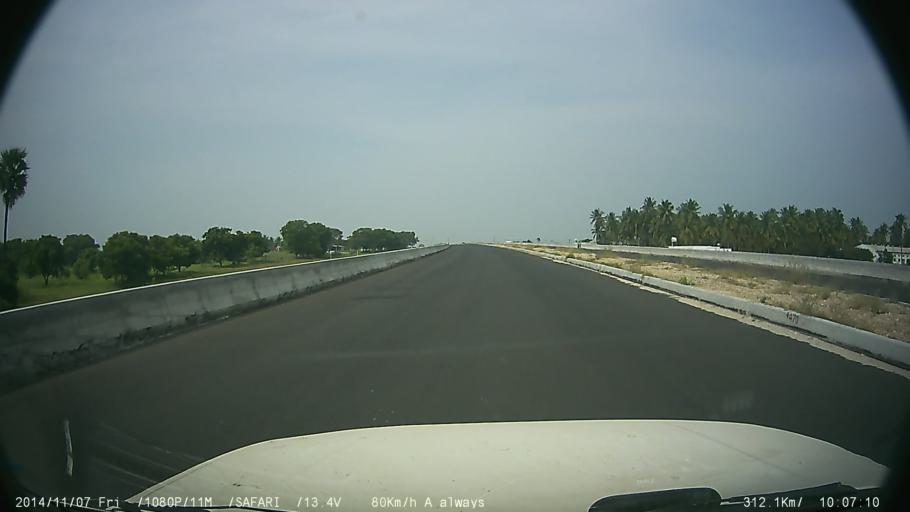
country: IN
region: Tamil Nadu
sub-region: Tiruppur
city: Avinashi
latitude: 11.2164
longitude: 77.3543
